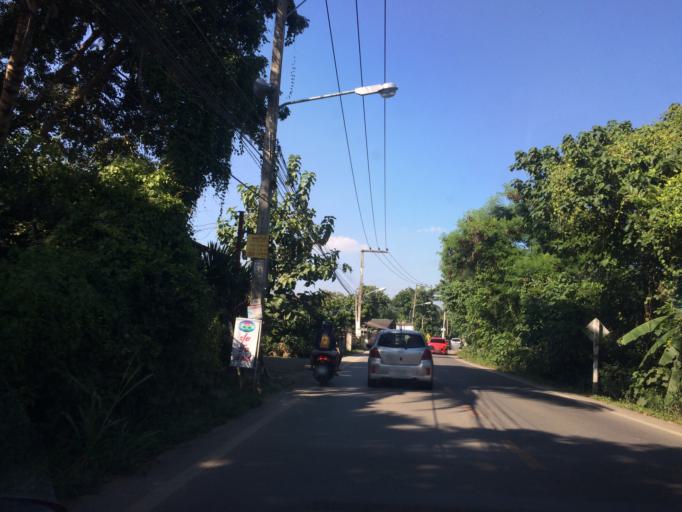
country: TH
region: Chiang Mai
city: Saraphi
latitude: 18.7234
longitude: 98.9860
